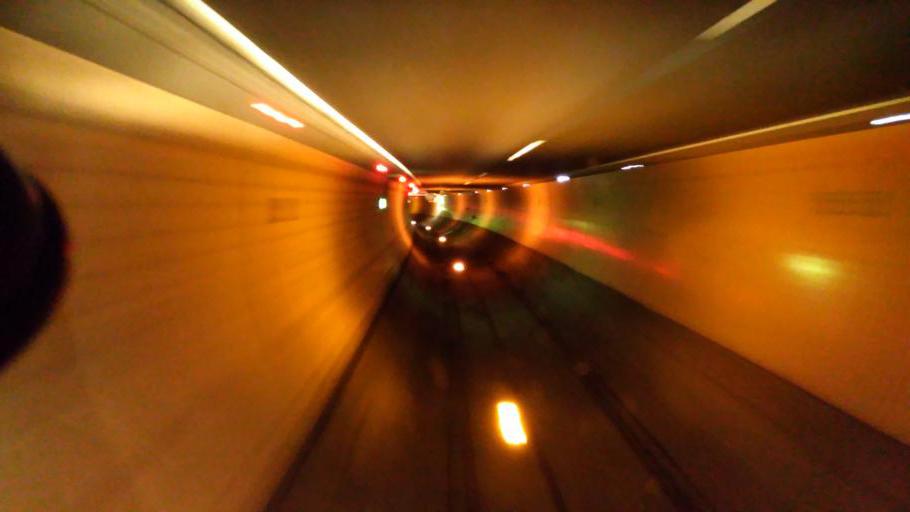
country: AT
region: Carinthia
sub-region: Politischer Bezirk Volkermarkt
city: Griffen
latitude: 46.6979
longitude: 14.7513
